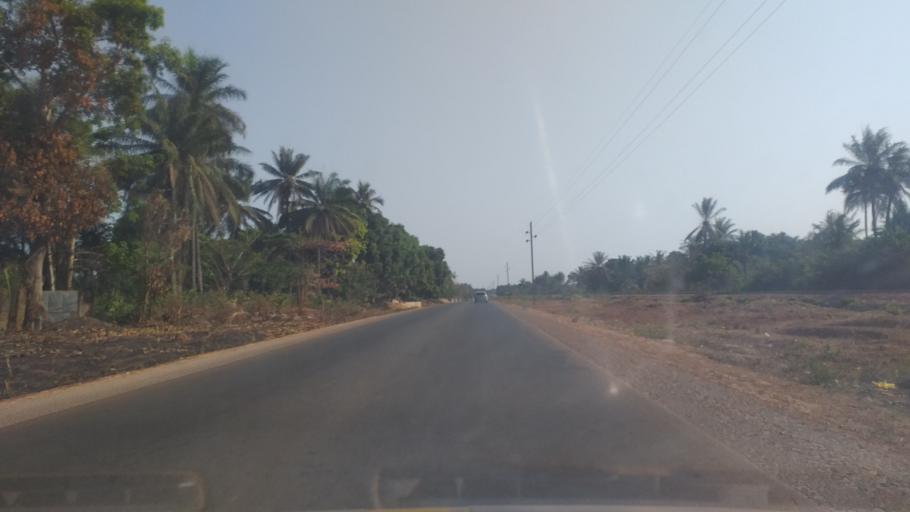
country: GN
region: Boke
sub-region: Boke Prefecture
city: Kamsar
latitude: 10.7244
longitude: -14.5194
